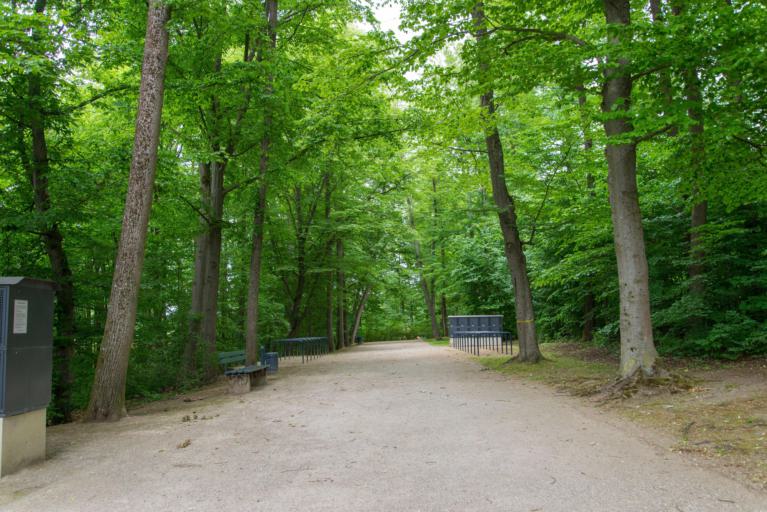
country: DE
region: Bavaria
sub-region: Upper Franconia
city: Bindlach
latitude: 49.9476
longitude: 11.6201
